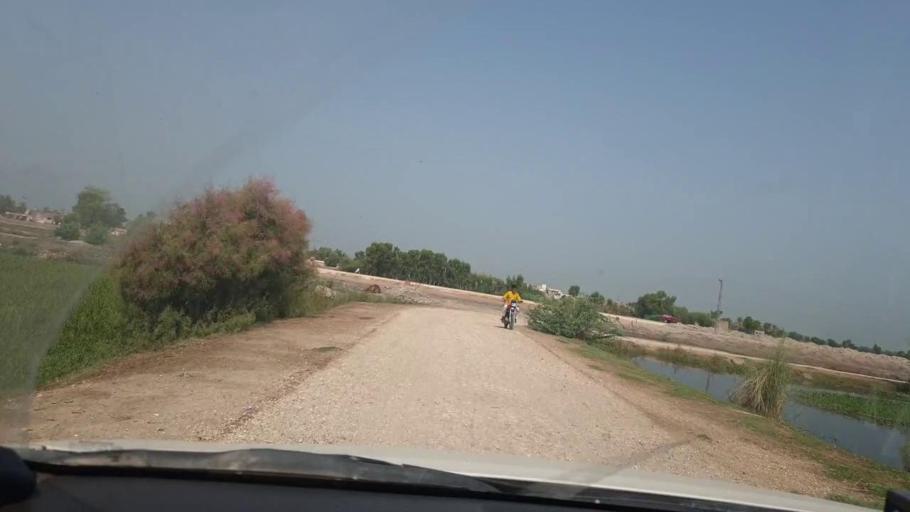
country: PK
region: Sindh
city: Chak
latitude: 27.8407
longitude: 68.7988
